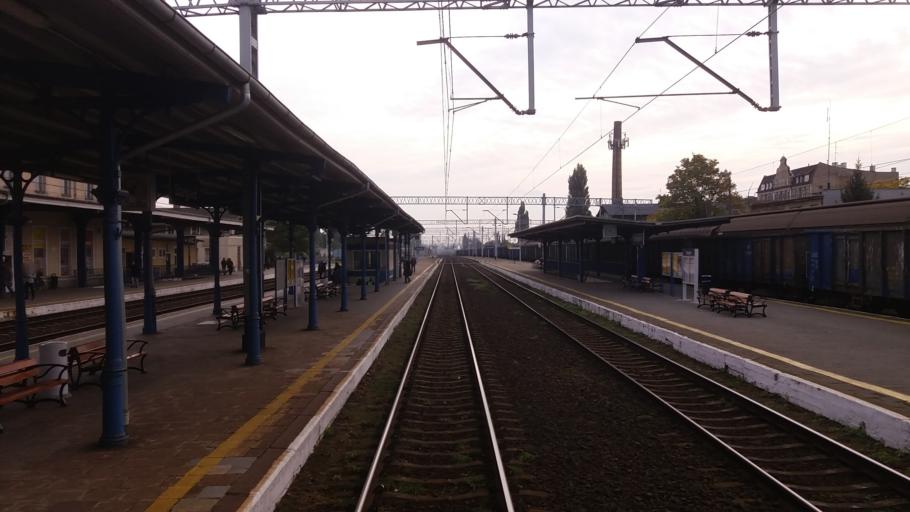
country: PL
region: West Pomeranian Voivodeship
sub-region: Powiat stargardzki
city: Stargard Szczecinski
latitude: 53.3395
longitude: 15.0311
